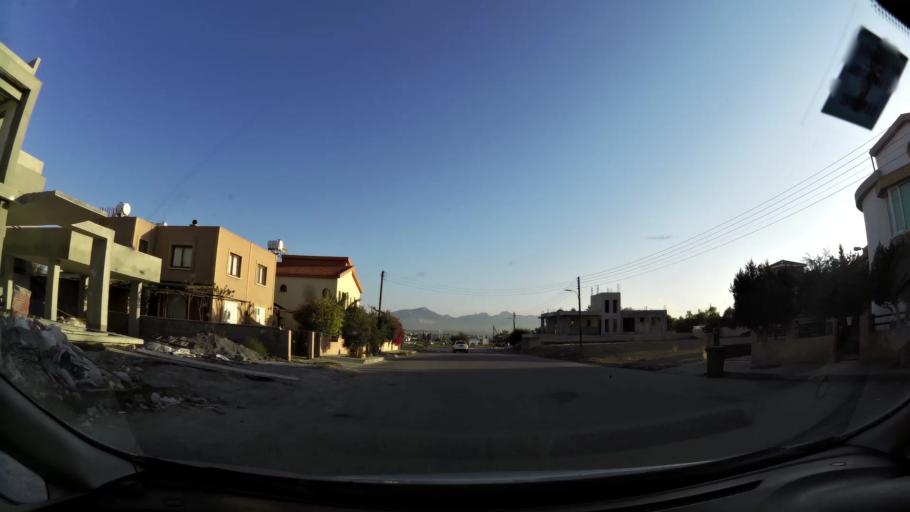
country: CY
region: Lefkosia
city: Nicosia
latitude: 35.1944
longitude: 33.3164
